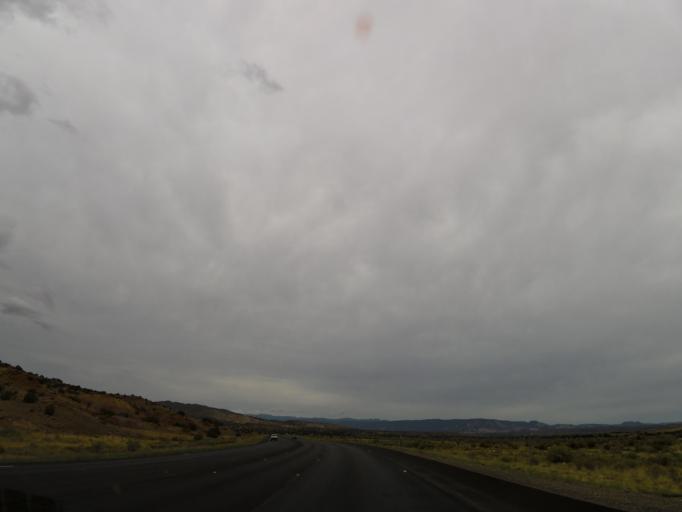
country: US
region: New Mexico
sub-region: Sandoval County
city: Jemez Pueblo
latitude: 35.5433
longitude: -106.8313
